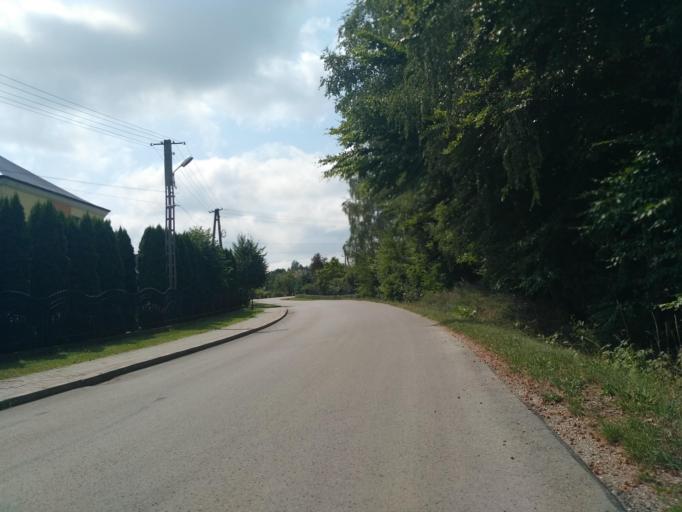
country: PL
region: Subcarpathian Voivodeship
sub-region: Powiat lancucki
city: Kraczkowa
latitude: 50.0159
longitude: 22.1658
